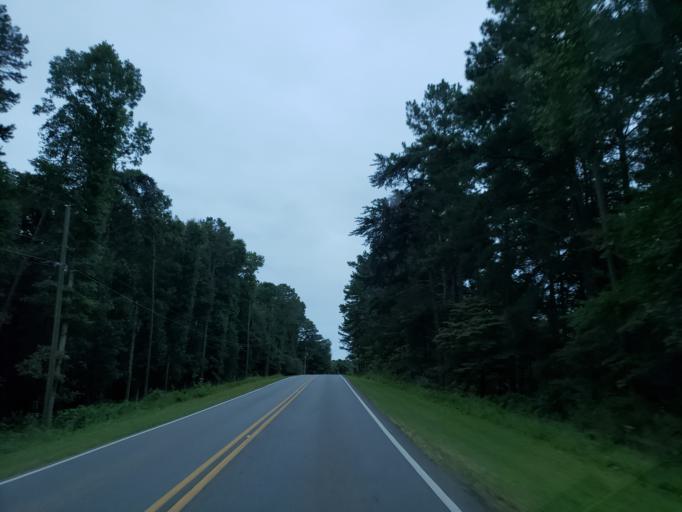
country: US
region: Georgia
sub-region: Cherokee County
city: Canton
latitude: 34.2852
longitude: -84.4528
